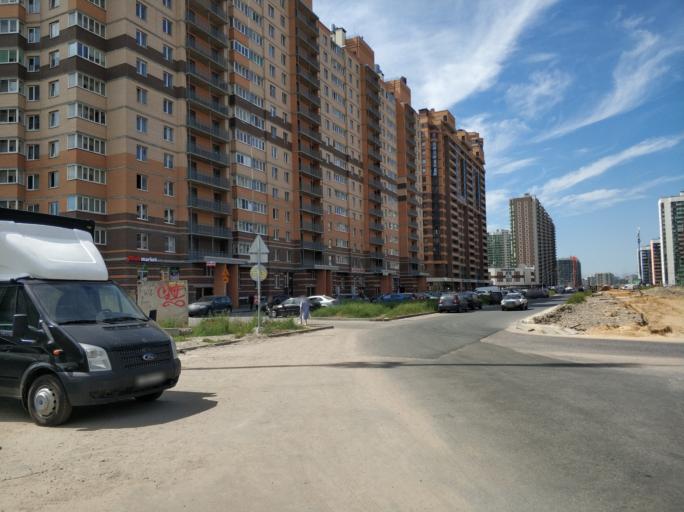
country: RU
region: Leningrad
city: Murino
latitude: 60.0568
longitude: 30.4345
